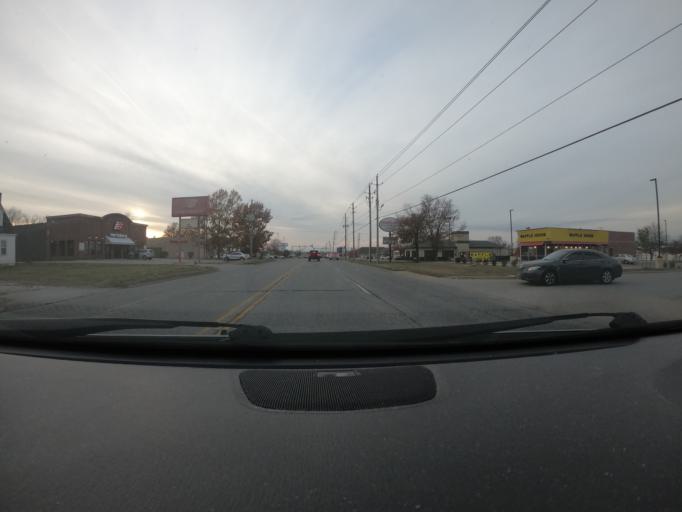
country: US
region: Arkansas
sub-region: Benton County
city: Rogers
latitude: 36.3340
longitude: -94.1415
